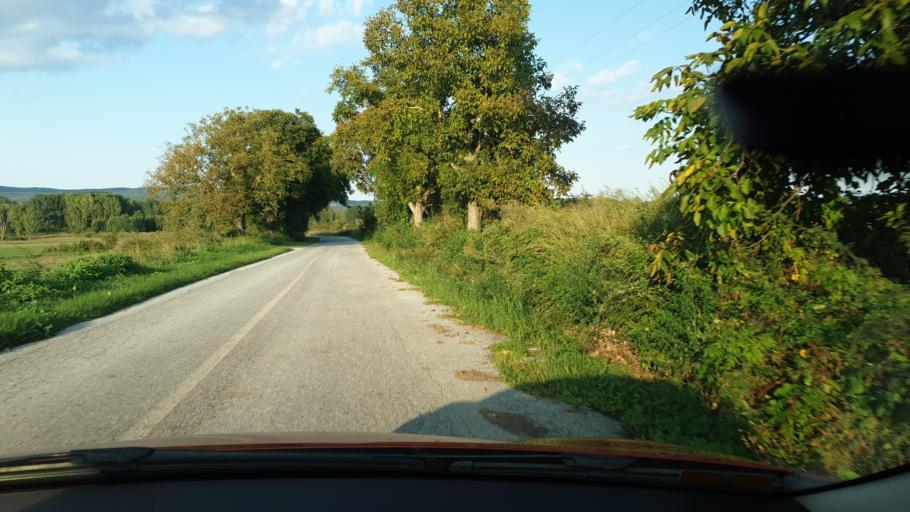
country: GR
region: Central Macedonia
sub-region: Nomos Chalkidikis
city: Galatista
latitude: 40.5576
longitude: 23.3061
